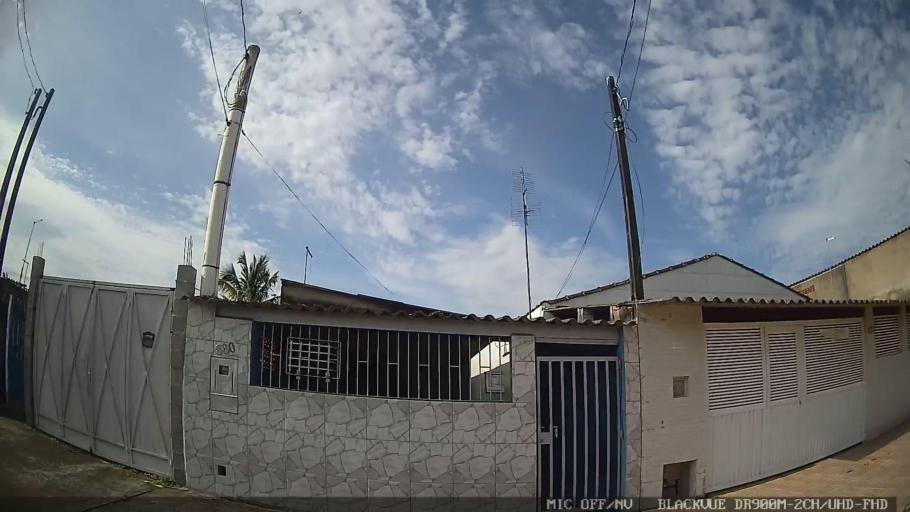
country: BR
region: Sao Paulo
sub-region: Itanhaem
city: Itanhaem
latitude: -24.1611
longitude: -46.7677
